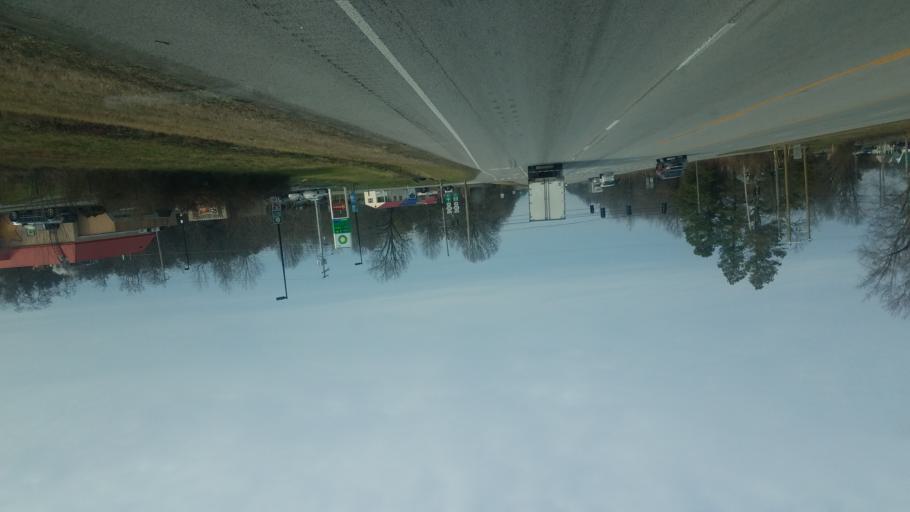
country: US
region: Kentucky
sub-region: Boyle County
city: Junction City
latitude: 37.5821
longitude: -84.7871
